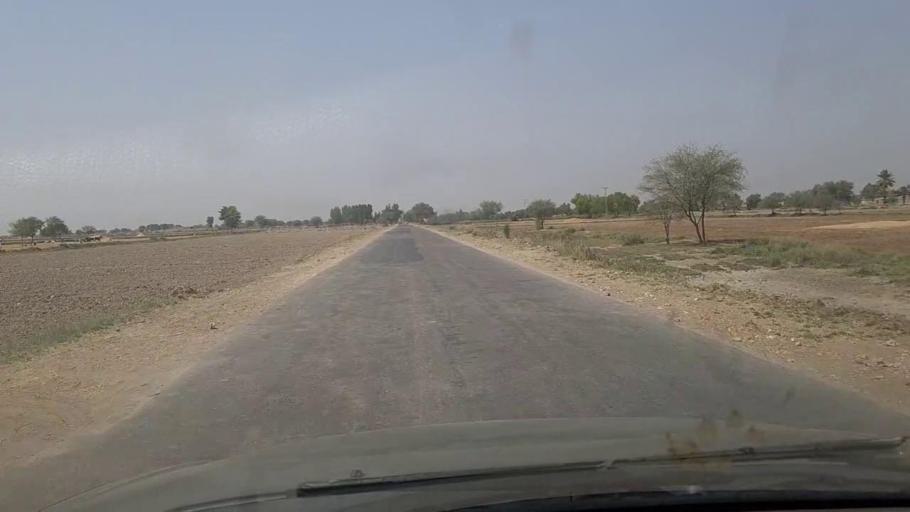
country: PK
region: Sindh
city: Khanpur
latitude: 27.8732
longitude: 69.4550
